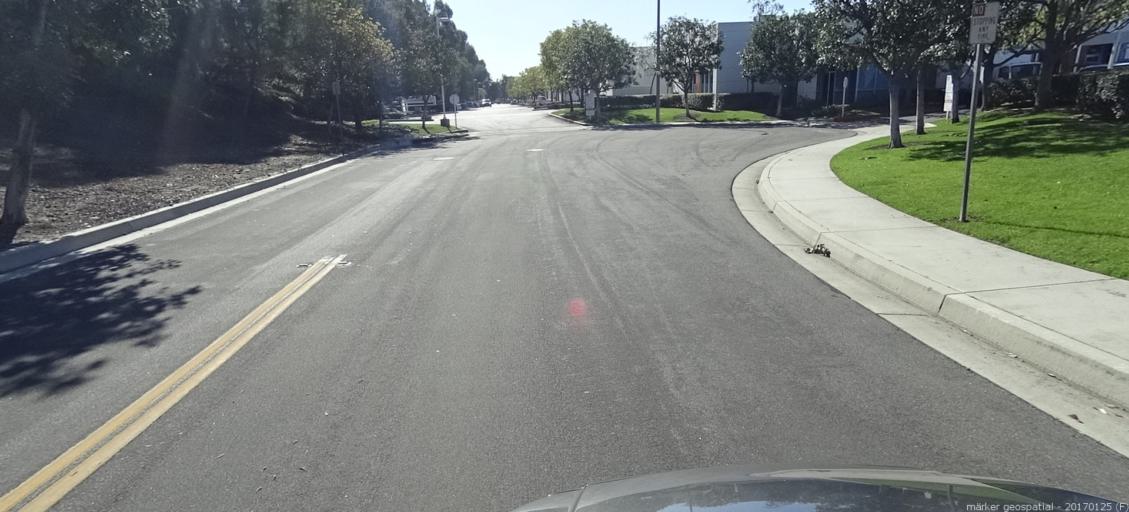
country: US
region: California
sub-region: Orange County
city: Lake Forest
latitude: 33.6575
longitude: -117.6986
